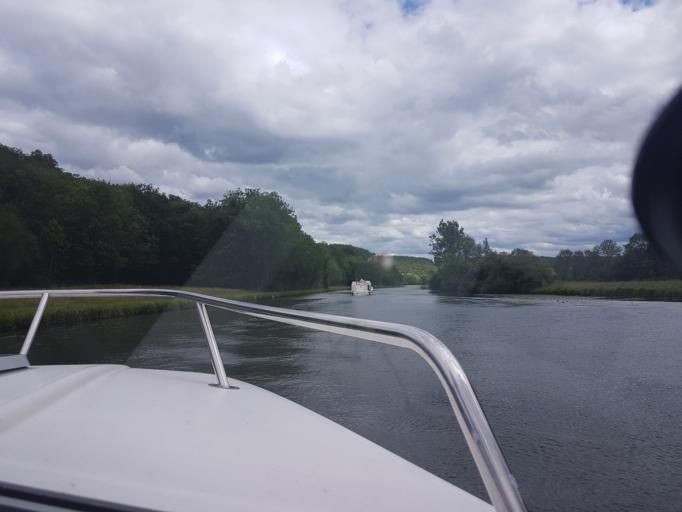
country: FR
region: Bourgogne
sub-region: Departement de l'Yonne
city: Vermenton
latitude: 47.5838
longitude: 3.6444
